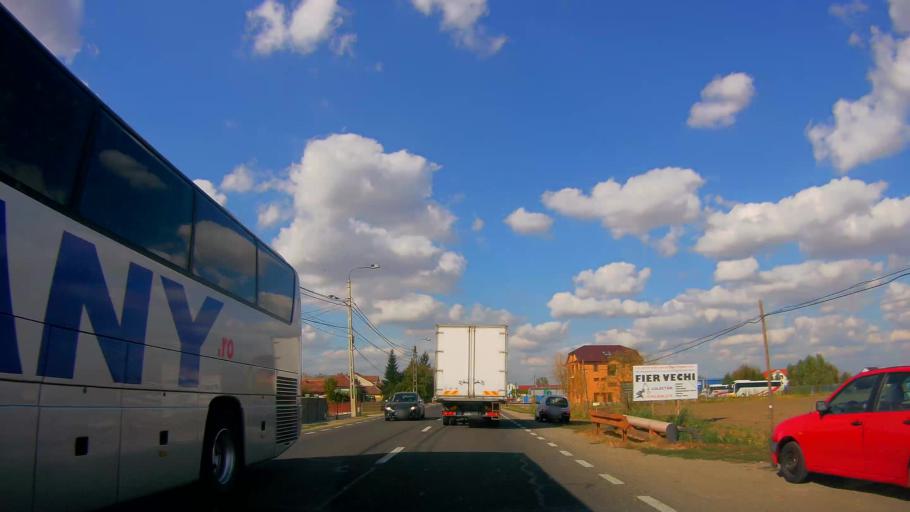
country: RO
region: Satu Mare
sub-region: Comuna Paulesti
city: Paulesti
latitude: 47.7514
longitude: 22.8831
